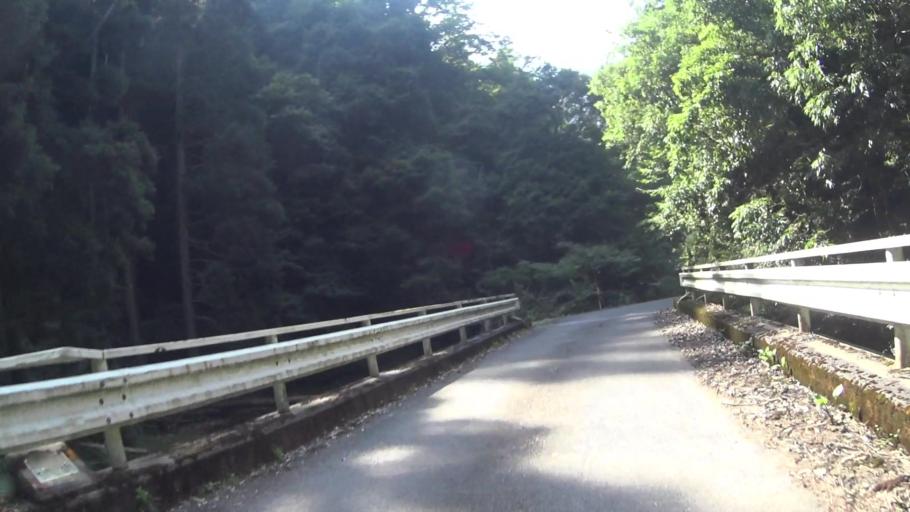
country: JP
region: Fukui
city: Obama
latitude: 35.2848
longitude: 135.6458
